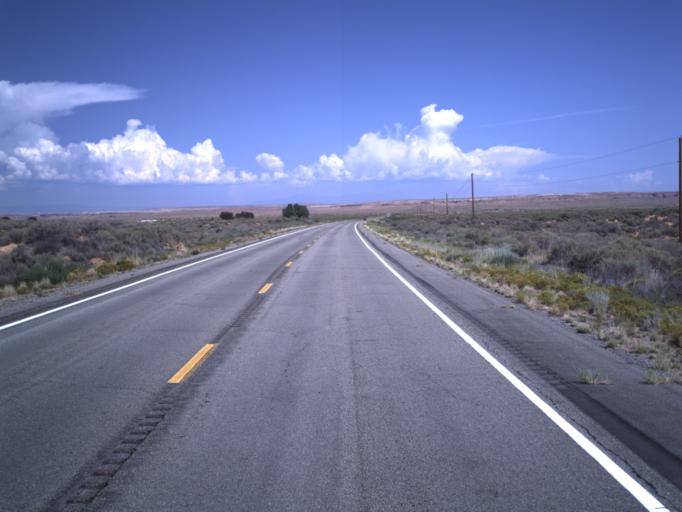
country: US
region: Utah
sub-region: San Juan County
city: Blanding
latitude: 37.0938
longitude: -109.5478
